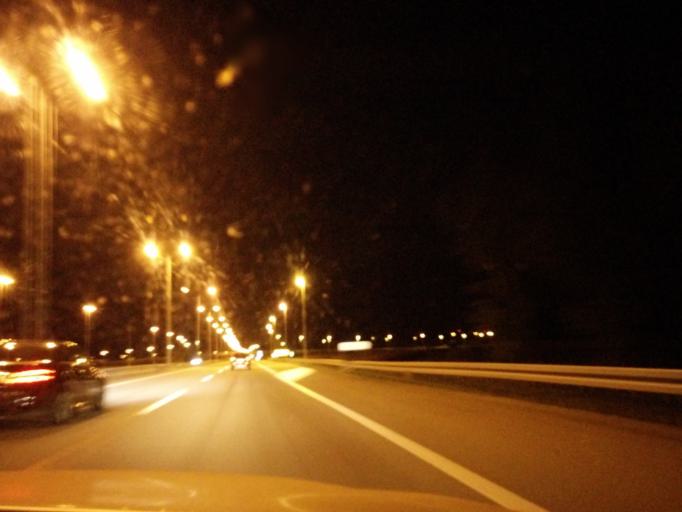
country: RS
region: Autonomna Pokrajina Vojvodina
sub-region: Sremski Okrug
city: Sremska Mitrovica
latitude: 44.9987
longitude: 19.6585
